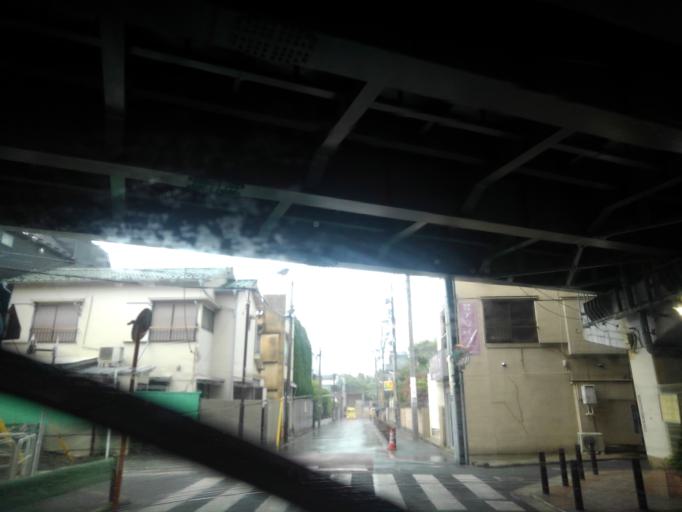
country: JP
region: Tokyo
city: Musashino
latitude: 35.7034
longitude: 139.5853
